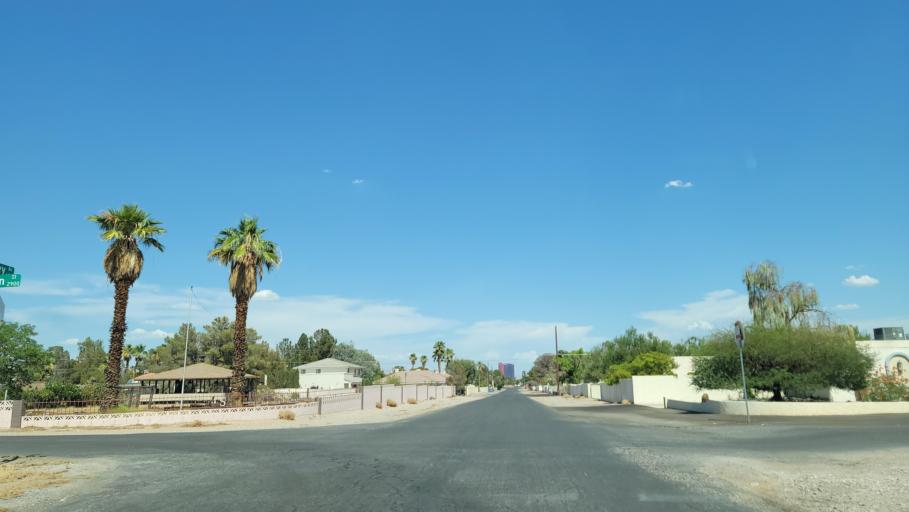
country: US
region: Nevada
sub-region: Clark County
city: Spring Valley
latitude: 36.1349
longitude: -115.2320
